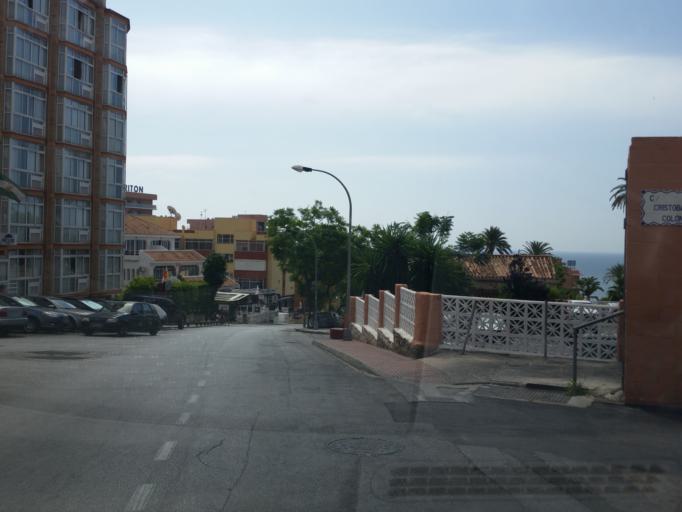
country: ES
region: Andalusia
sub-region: Provincia de Malaga
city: Torremolinos
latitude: 36.5971
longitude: -4.5213
